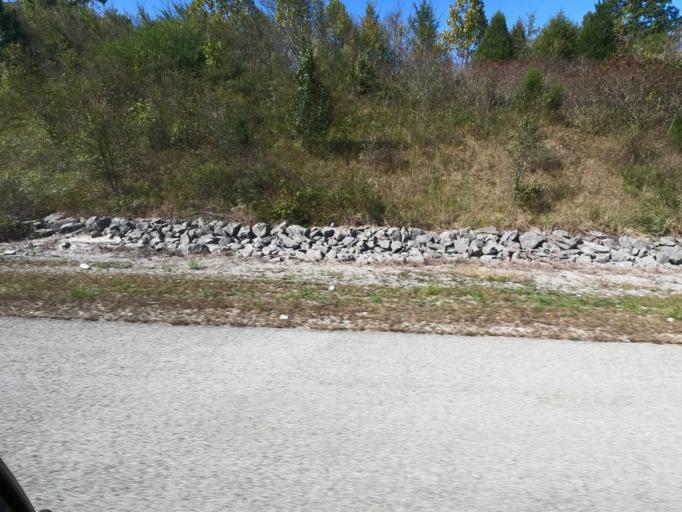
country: US
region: Tennessee
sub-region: Maury County
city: Mount Pleasant
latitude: 35.4685
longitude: -87.2655
